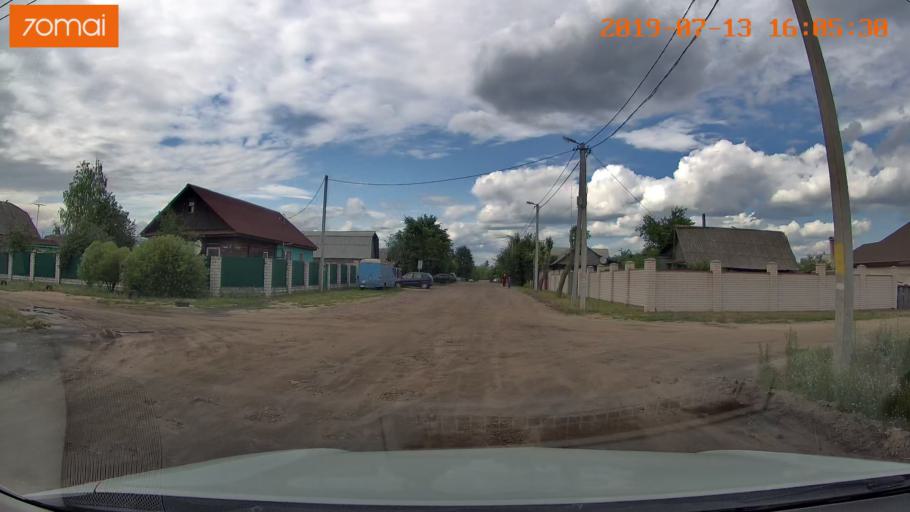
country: BY
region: Mogilev
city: Babruysk
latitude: 53.1490
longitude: 29.2052
